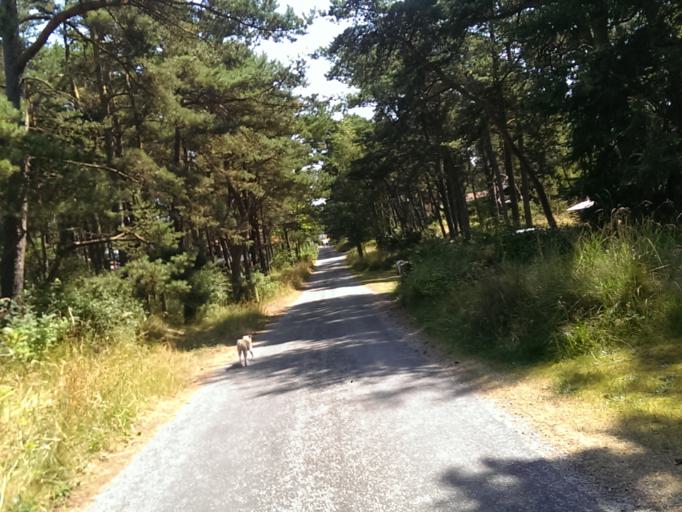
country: SE
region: Skane
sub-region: Simrishamns Kommun
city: Simrishamn
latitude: 55.4285
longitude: 14.2264
